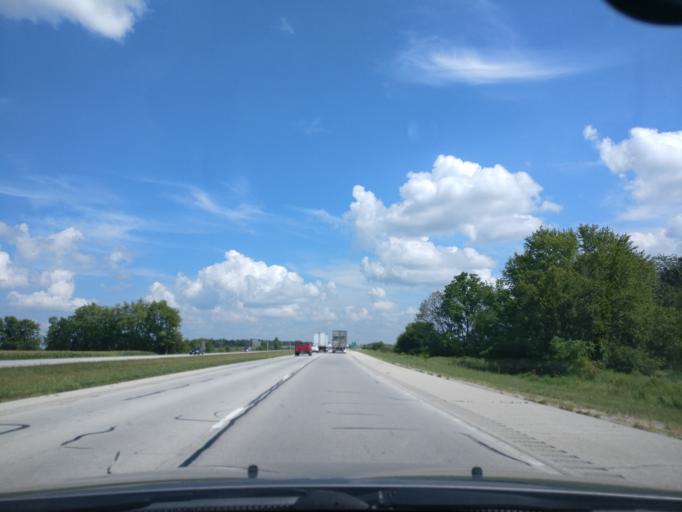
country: US
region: Ohio
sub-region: Greene County
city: Jamestown
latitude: 39.6726
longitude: -83.7483
